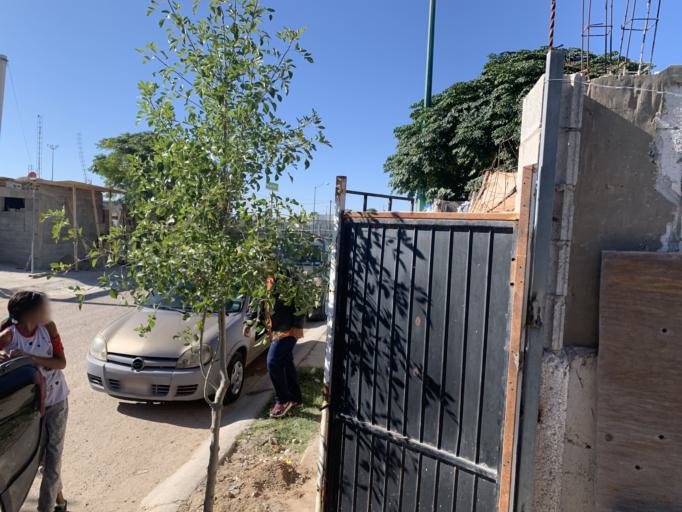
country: US
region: Texas
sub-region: El Paso County
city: San Elizario
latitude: 31.5699
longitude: -106.3432
